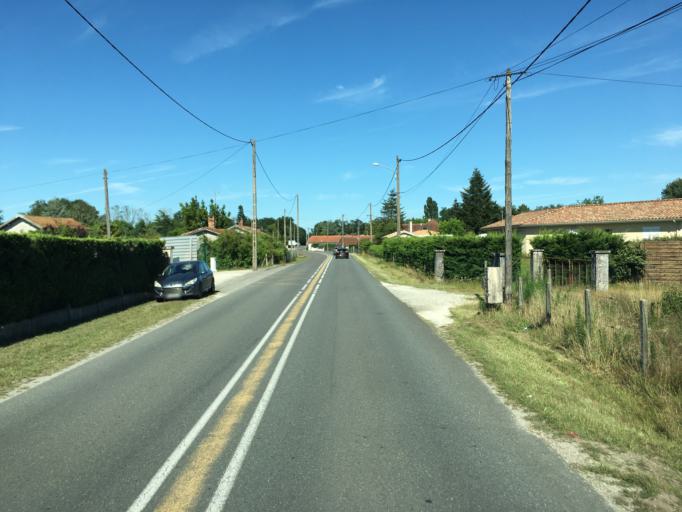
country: FR
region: Aquitaine
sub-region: Departement de la Gironde
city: Belin-Beliet
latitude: 44.5084
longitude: -0.7832
